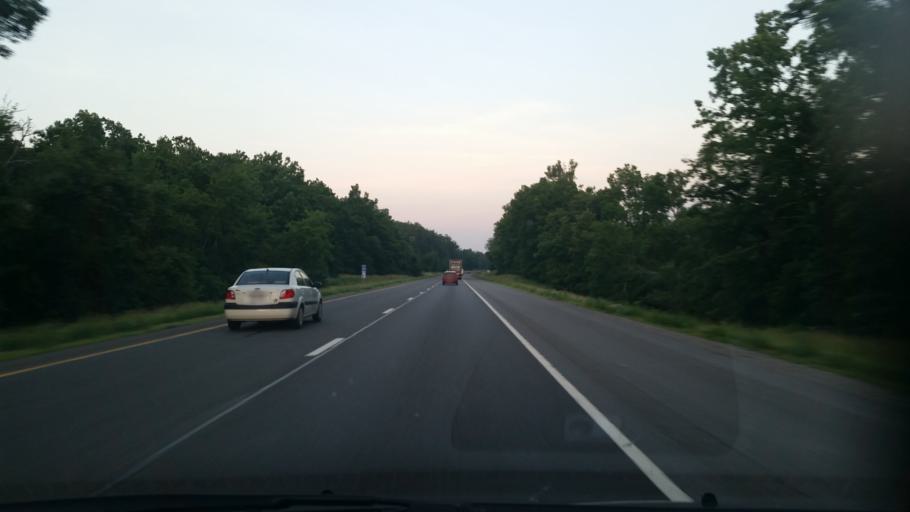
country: US
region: Tennessee
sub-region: Cumberland County
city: Crossville
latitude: 36.0442
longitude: -85.1223
